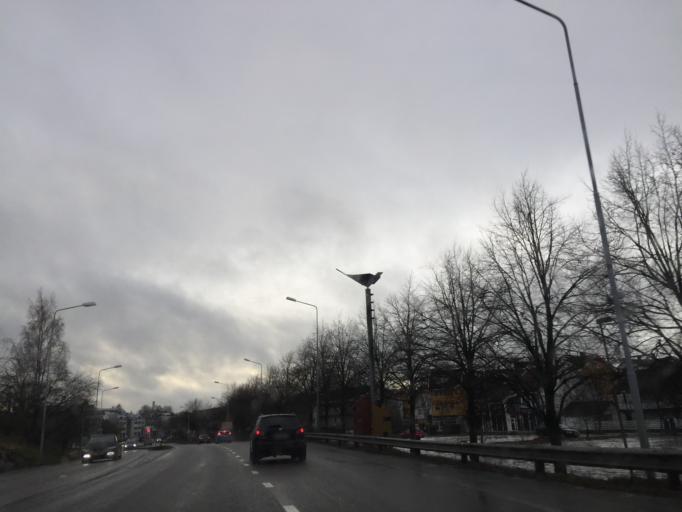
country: NO
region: Ostfold
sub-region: Moss
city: Moss
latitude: 59.4375
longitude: 10.6727
